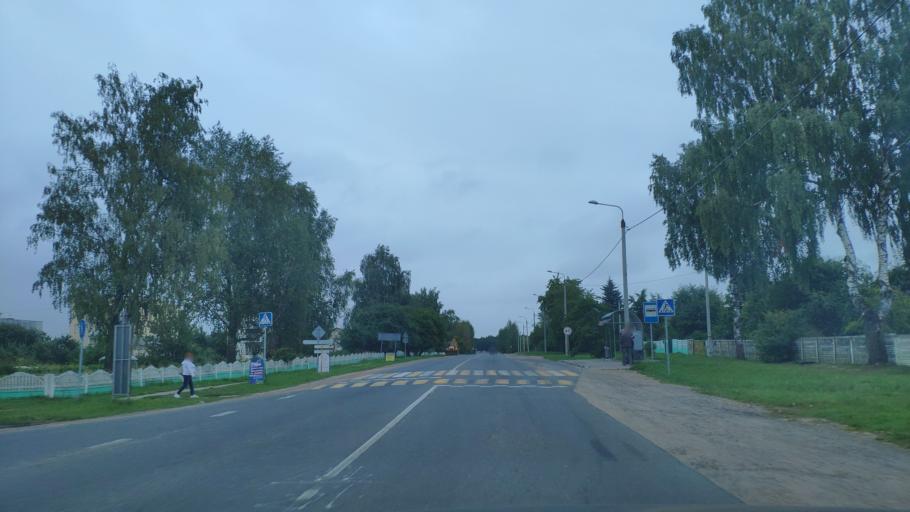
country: BY
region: Minsk
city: Azyartso
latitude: 53.8407
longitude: 27.3930
